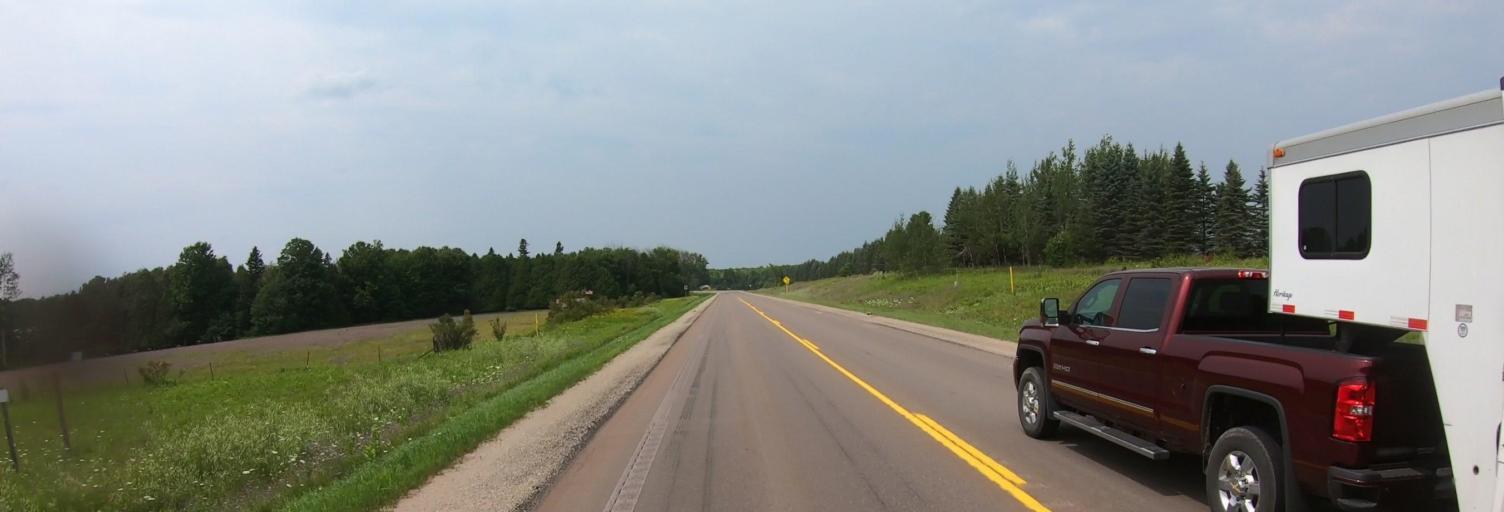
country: US
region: Michigan
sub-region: Alger County
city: Munising
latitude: 46.3496
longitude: -86.9507
